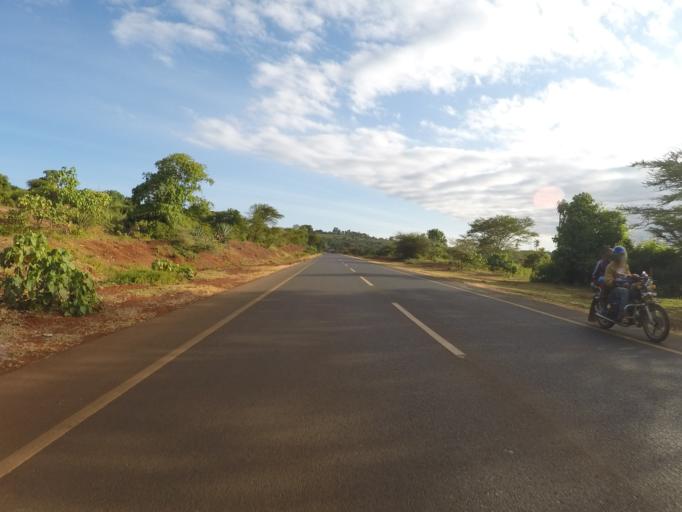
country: TZ
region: Arusha
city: Kiratu
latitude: -3.3318
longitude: 35.7086
